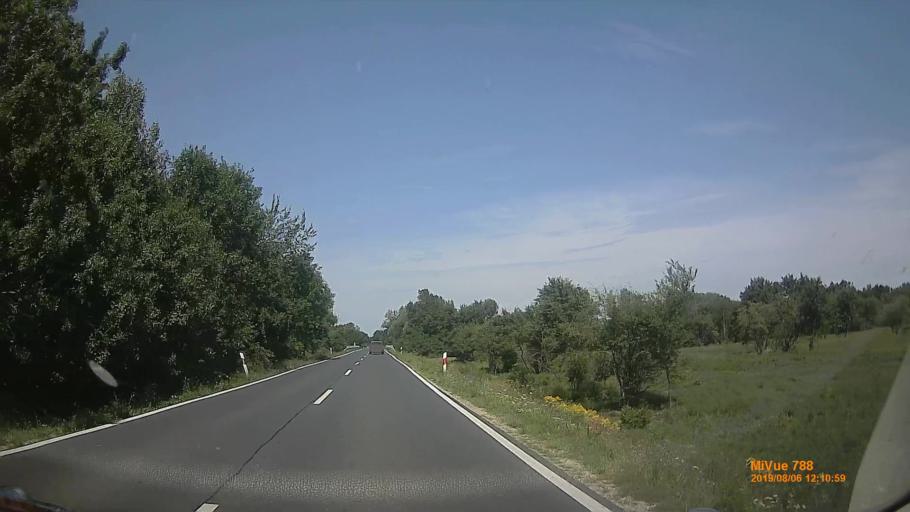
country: HU
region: Vas
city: Vasvar
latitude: 47.1079
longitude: 16.8661
